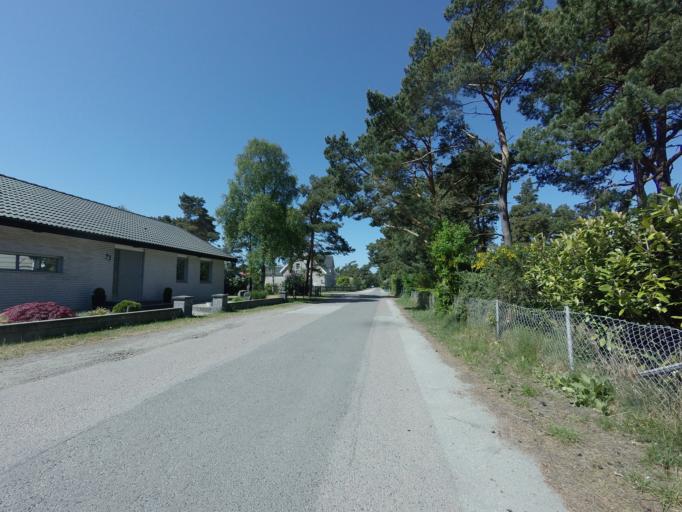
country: SE
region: Skane
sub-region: Vellinge Kommun
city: Hollviken
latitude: 55.4084
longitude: 12.9522
